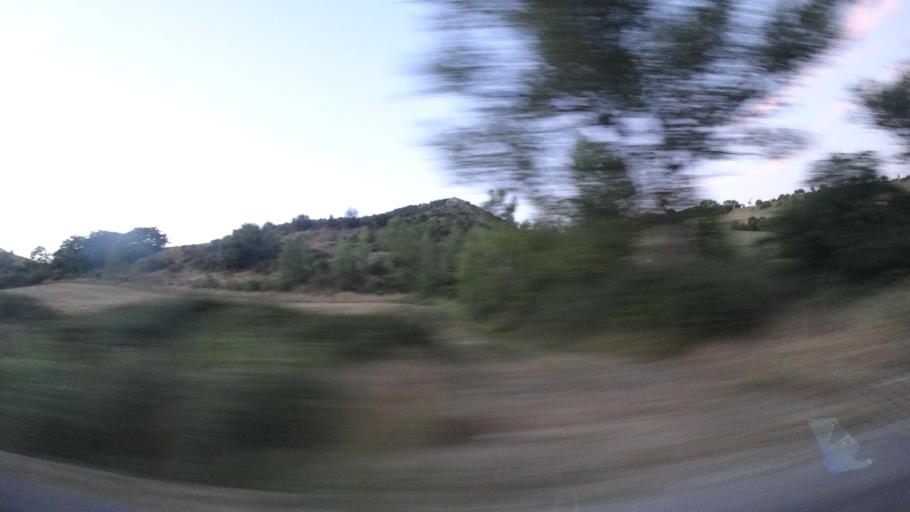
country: FR
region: Midi-Pyrenees
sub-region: Departement de l'Aveyron
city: Millau
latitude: 44.1279
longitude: 3.0537
